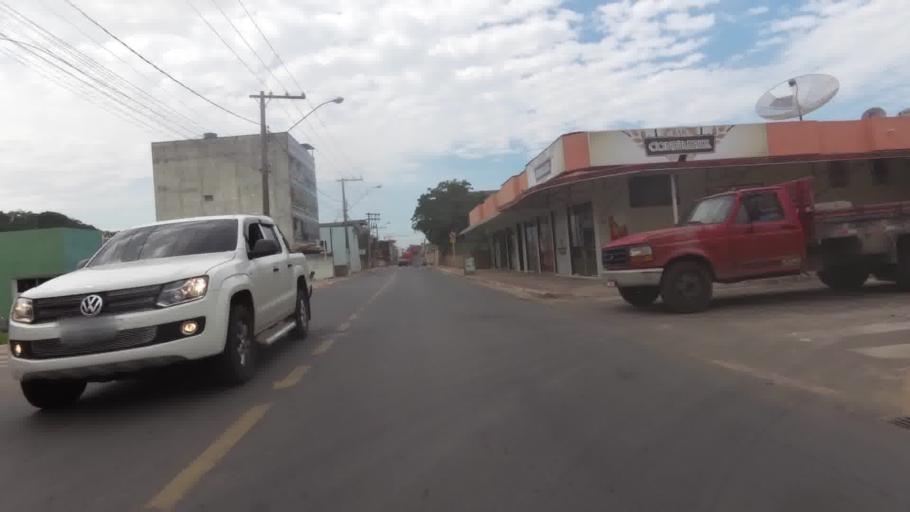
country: BR
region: Espirito Santo
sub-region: Piuma
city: Piuma
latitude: -20.8411
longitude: -40.7418
